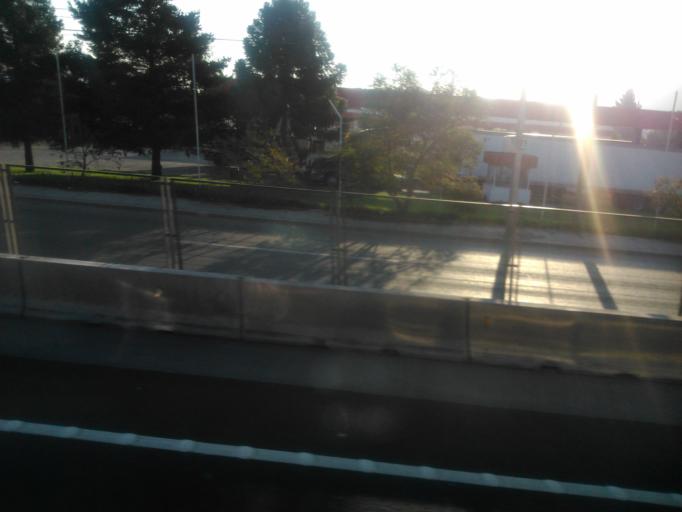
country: CL
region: Santiago Metropolitan
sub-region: Provincia de Maipo
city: San Bernardo
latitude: -33.6143
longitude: -70.7161
